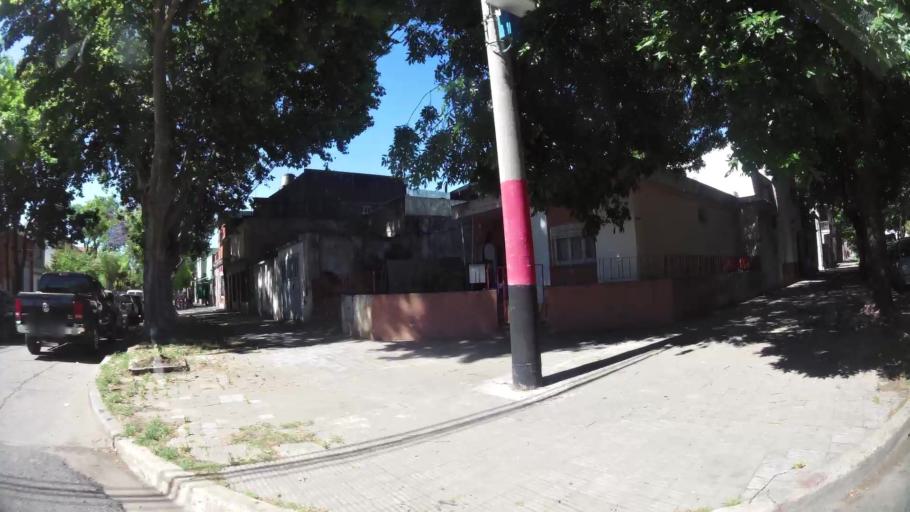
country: AR
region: Santa Fe
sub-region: Departamento de Rosario
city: Rosario
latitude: -32.9464
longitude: -60.6881
